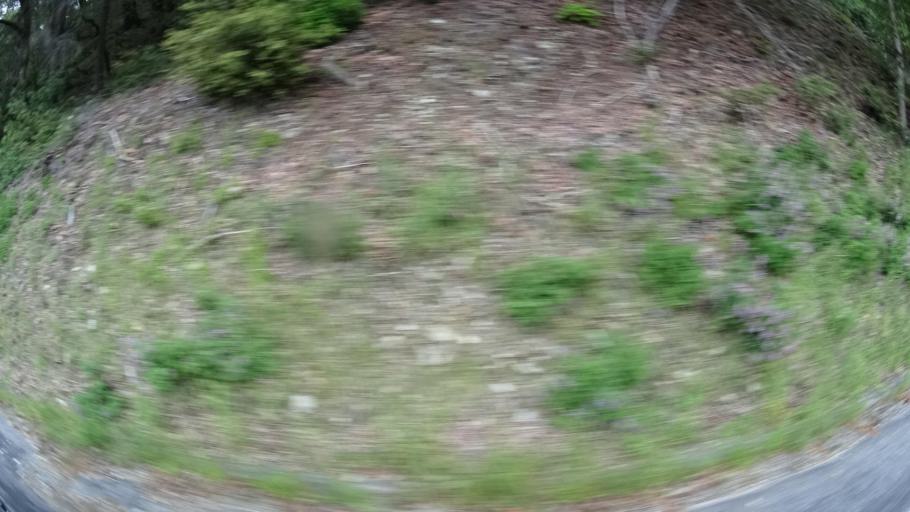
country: US
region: California
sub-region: Humboldt County
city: Willow Creek
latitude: 41.2515
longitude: -123.6382
